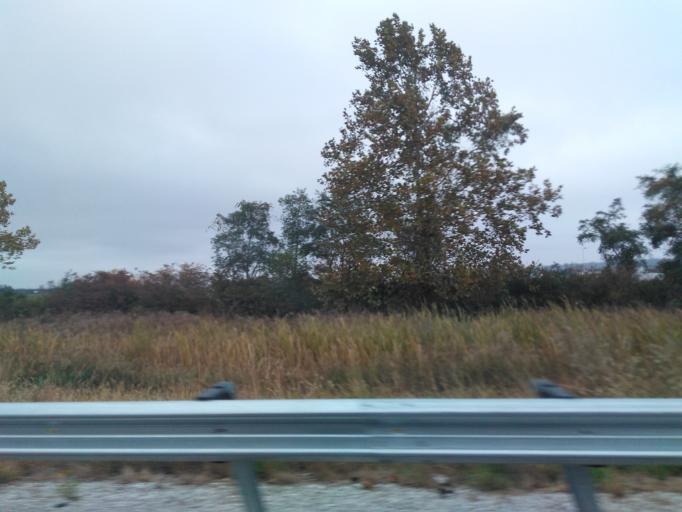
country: US
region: Illinois
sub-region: Saint Clair County
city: Caseyville
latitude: 38.6751
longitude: -90.0242
